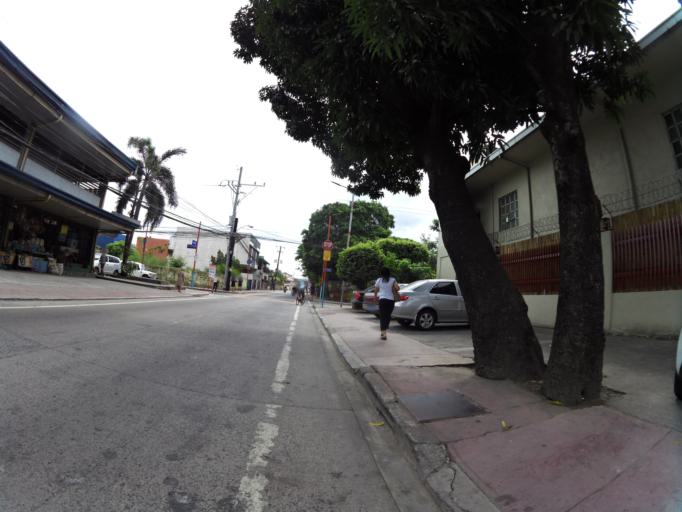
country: PH
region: Calabarzon
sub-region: Province of Rizal
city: Antipolo
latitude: 14.6419
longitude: 121.1114
